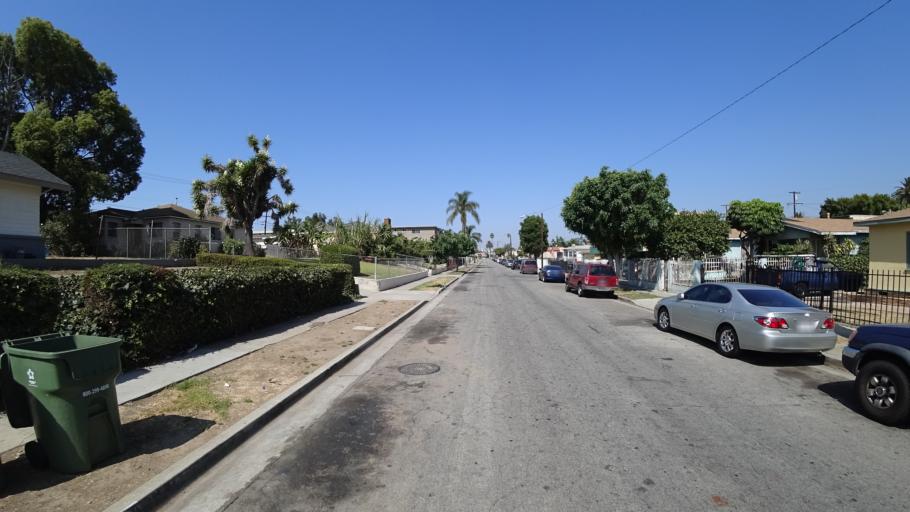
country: US
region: California
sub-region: Los Angeles County
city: Westmont
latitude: 33.9423
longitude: -118.3010
